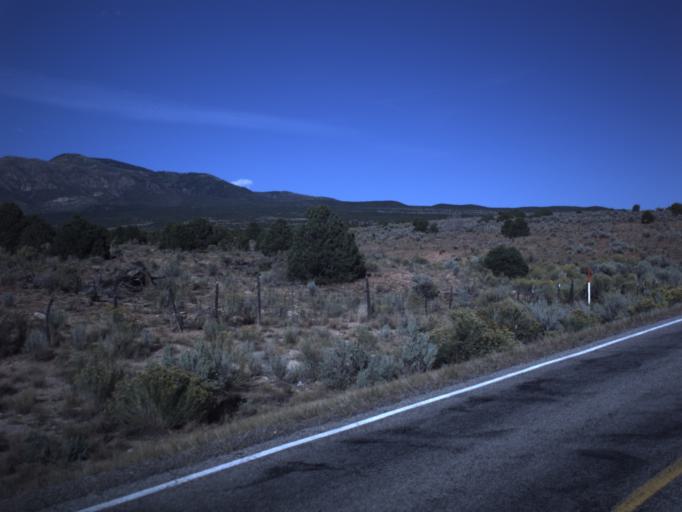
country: US
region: Utah
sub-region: Grand County
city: Moab
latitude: 38.3191
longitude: -109.3290
